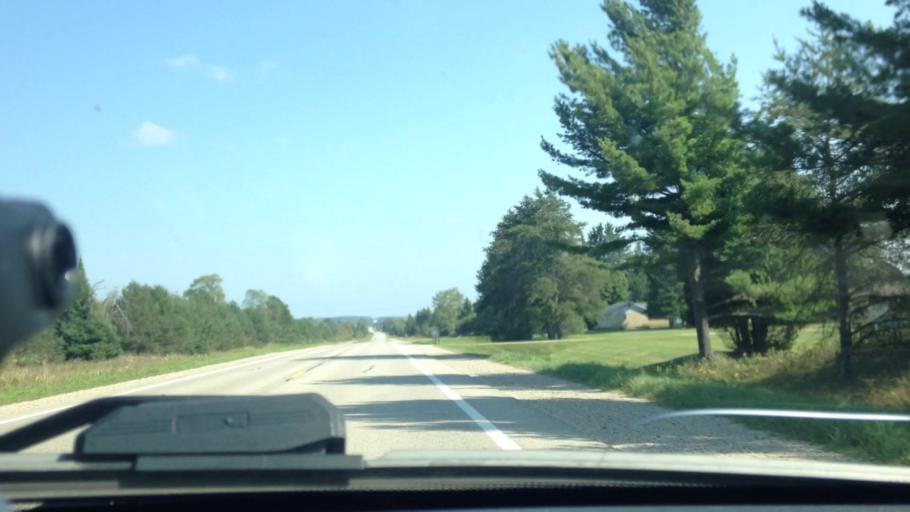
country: US
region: Michigan
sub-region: Luce County
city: Newberry
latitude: 46.3102
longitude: -85.6315
